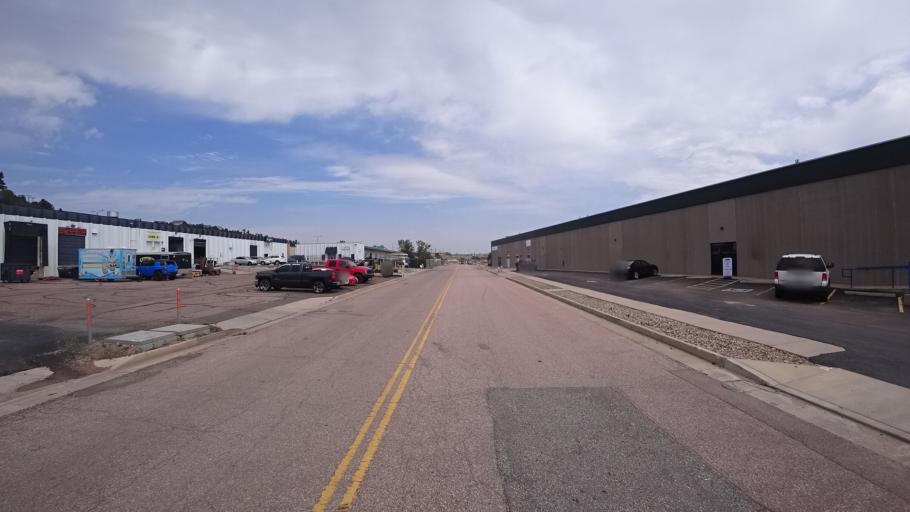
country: US
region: Colorado
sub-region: El Paso County
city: Colorado Springs
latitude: 38.9031
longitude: -104.8259
